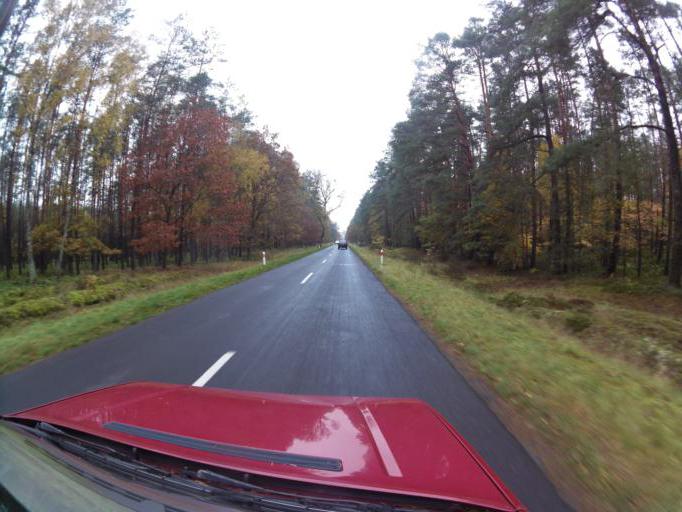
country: PL
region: West Pomeranian Voivodeship
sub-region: Powiat policki
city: Dobra
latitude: 53.5657
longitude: 14.4418
